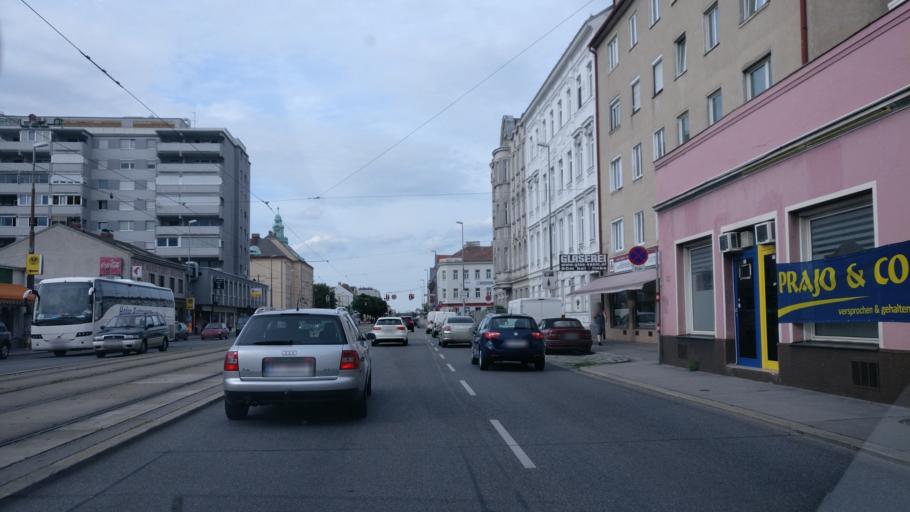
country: AT
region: Lower Austria
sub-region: Politischer Bezirk Korneuburg
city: Hagenbrunn
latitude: 48.2753
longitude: 16.4080
